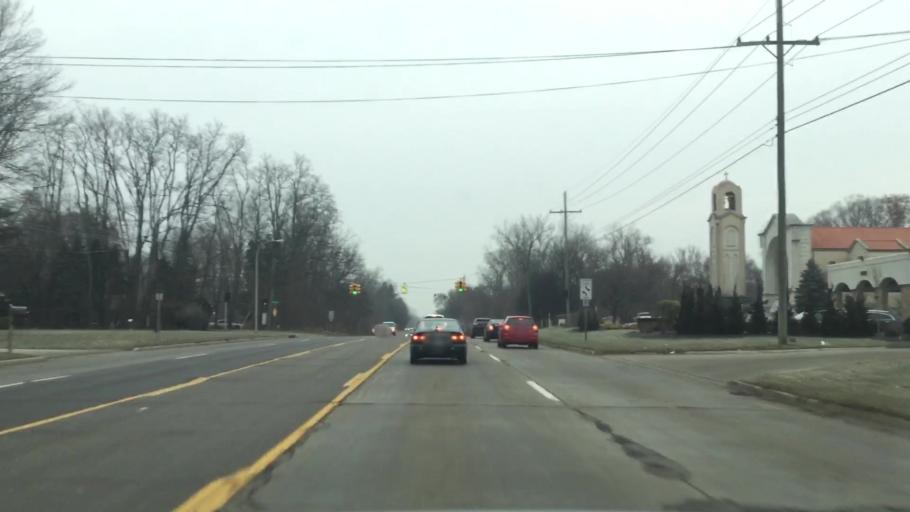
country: US
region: Michigan
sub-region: Wayne County
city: Livonia
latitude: 42.4183
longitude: -83.3549
